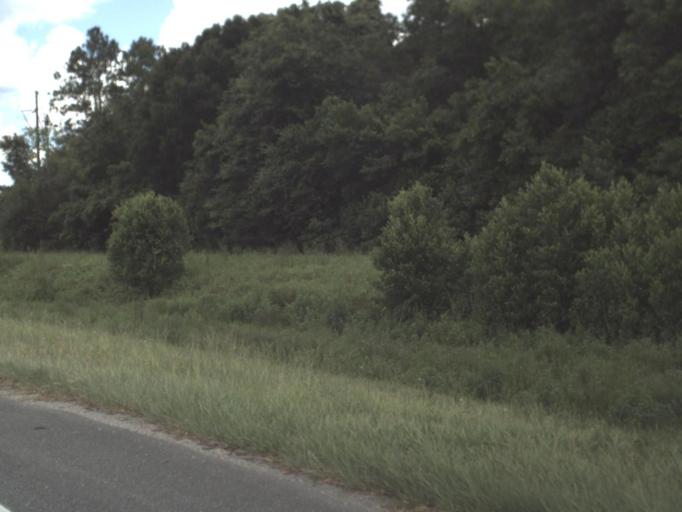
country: US
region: Florida
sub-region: Taylor County
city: Perry
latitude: 30.1212
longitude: -83.5919
